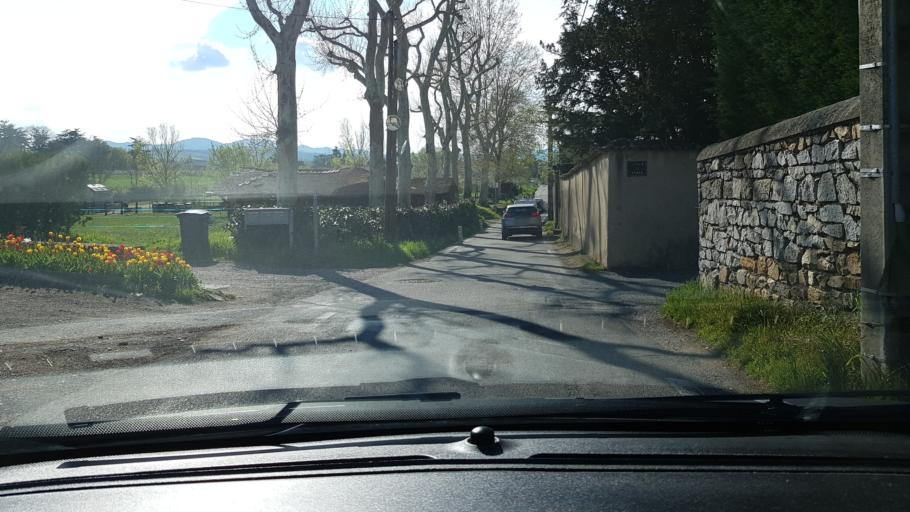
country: FR
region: Rhone-Alpes
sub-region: Departement du Rhone
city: Orlienas
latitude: 45.6643
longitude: 4.7240
